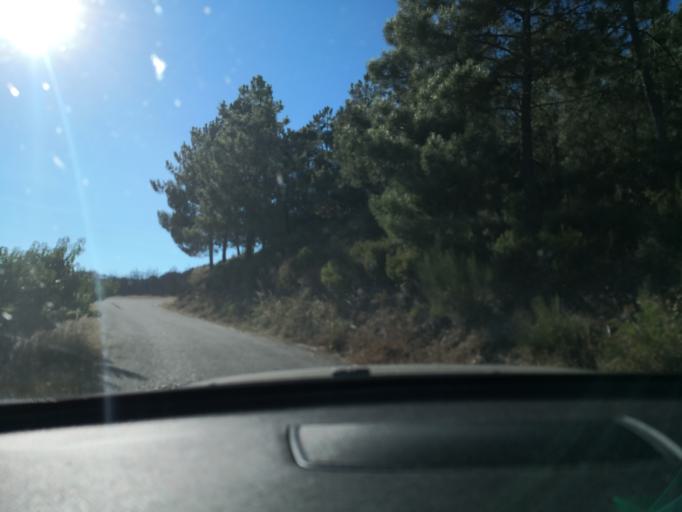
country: PT
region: Vila Real
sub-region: Sabrosa
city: Vilela
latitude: 41.2243
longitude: -7.5906
